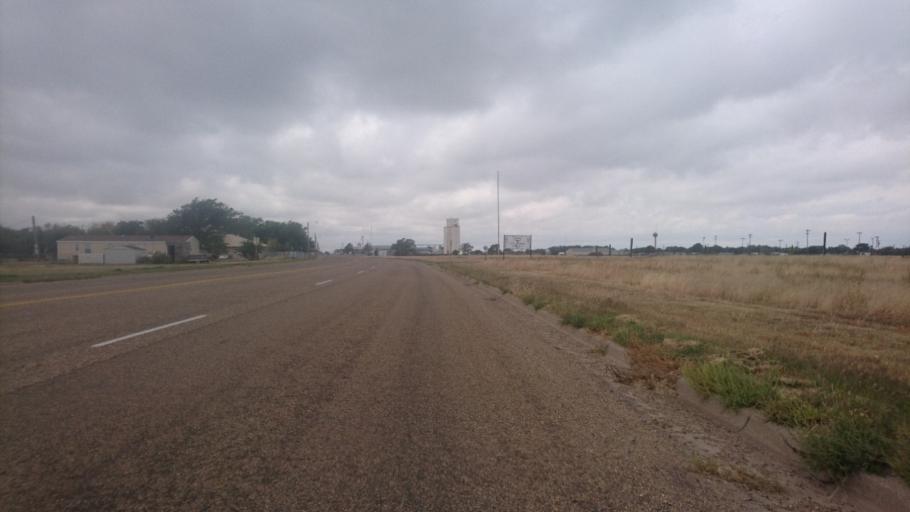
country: US
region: Texas
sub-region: Oldham County
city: Vega
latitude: 35.2429
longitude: -102.4182
